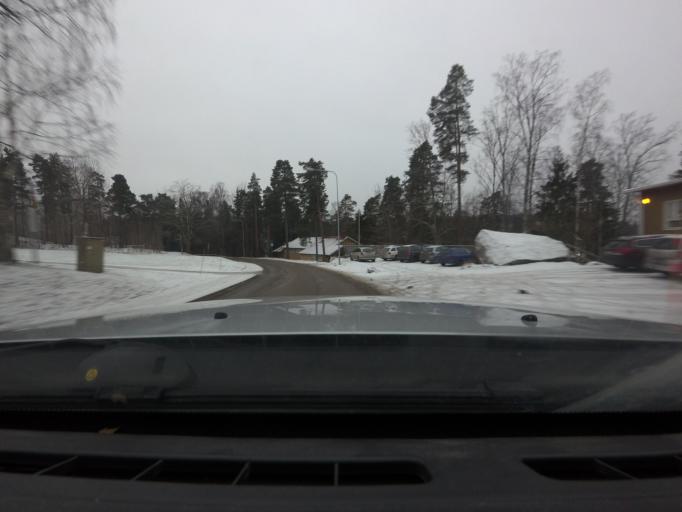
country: FI
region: Uusimaa
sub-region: Helsinki
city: Kauniainen
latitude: 60.2276
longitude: 24.7297
